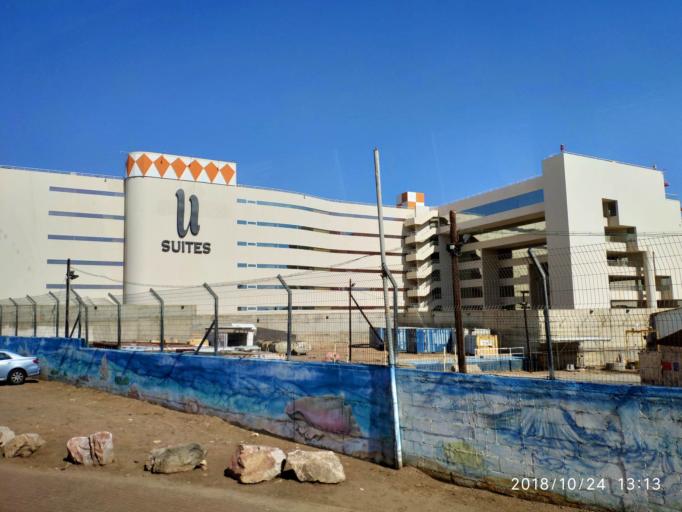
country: IL
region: Southern District
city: Eilat
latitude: 29.5464
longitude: 34.9517
